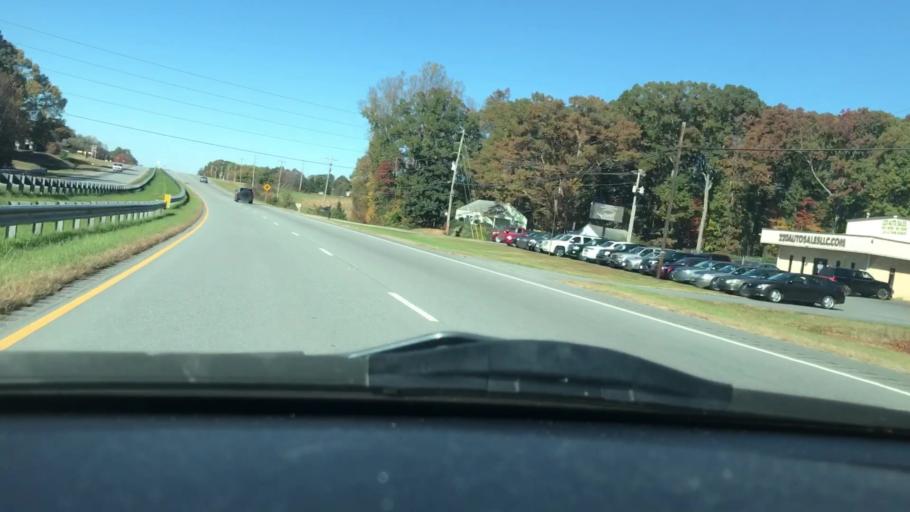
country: US
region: North Carolina
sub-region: Rockingham County
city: Madison
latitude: 36.3417
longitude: -79.9435
